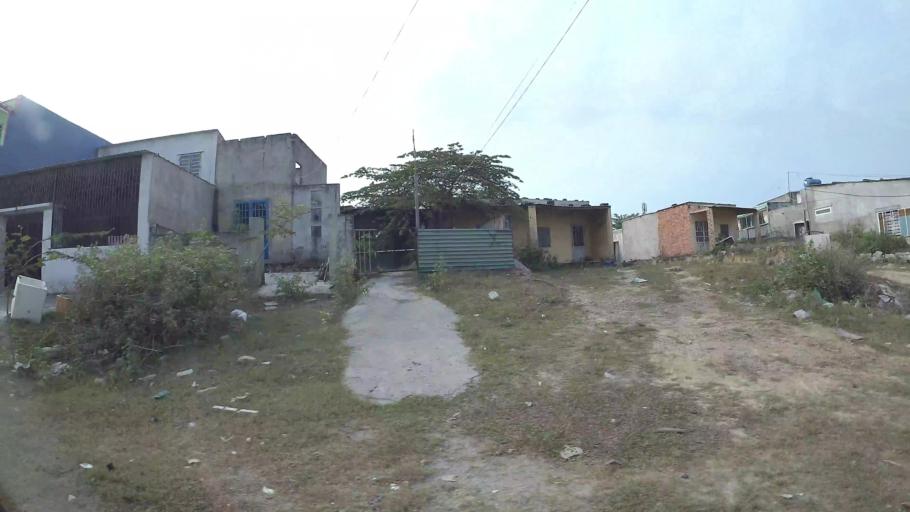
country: VN
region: Da Nang
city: Lien Chieu
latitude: 16.0491
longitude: 108.1534
